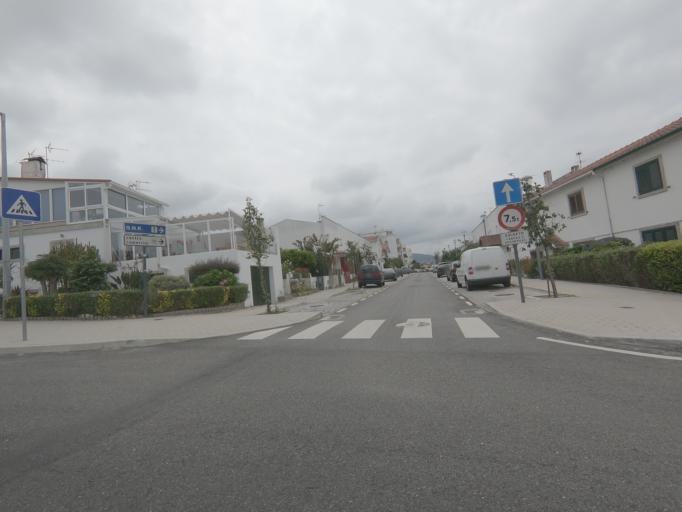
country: PT
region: Viana do Castelo
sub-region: Vila Nova de Cerveira
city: Vila Nova de Cerveira
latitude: 41.9447
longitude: -8.7421
